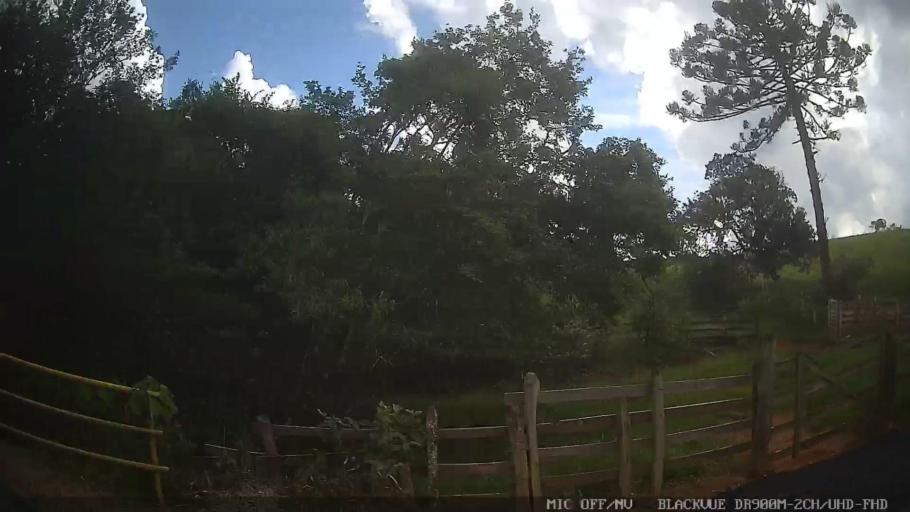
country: BR
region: Minas Gerais
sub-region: Extrema
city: Extrema
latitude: -22.8322
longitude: -46.2301
